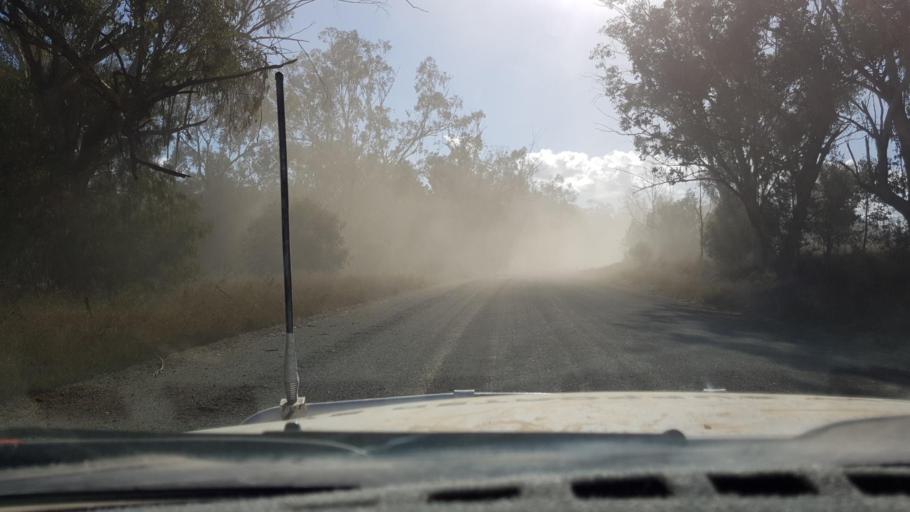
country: AU
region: New South Wales
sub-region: Narrabri
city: Blair Athol
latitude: -30.6664
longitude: 150.3452
